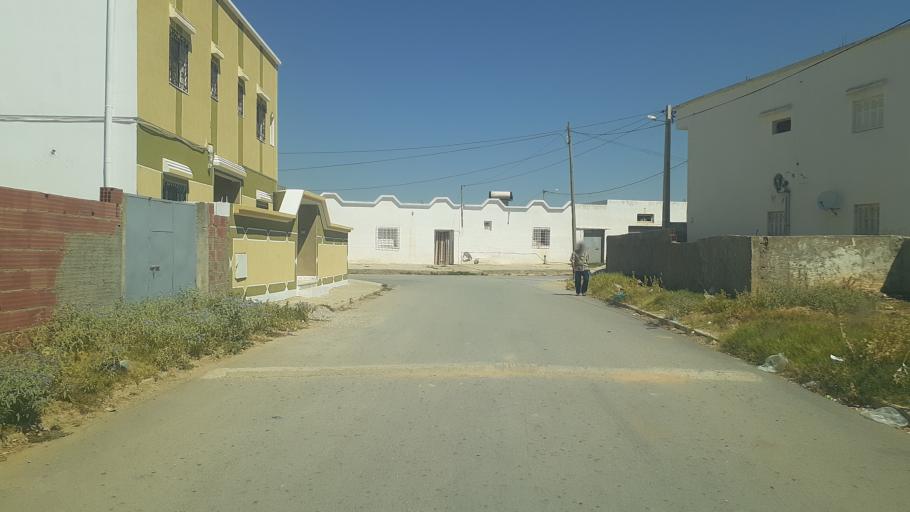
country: TN
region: Al Qayrawan
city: Sbikha
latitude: 36.1183
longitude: 10.0892
